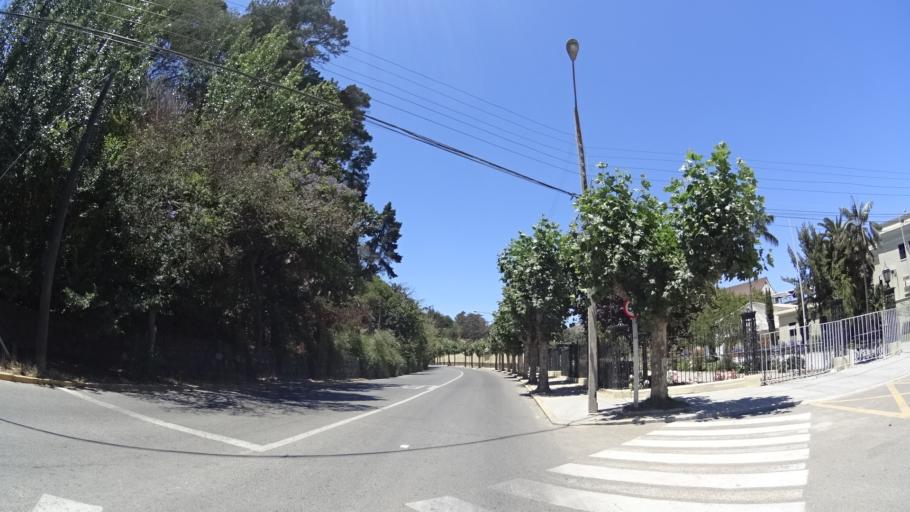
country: CL
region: Valparaiso
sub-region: Provincia de Valparaiso
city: Vina del Mar
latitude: -33.0189
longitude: -71.5392
